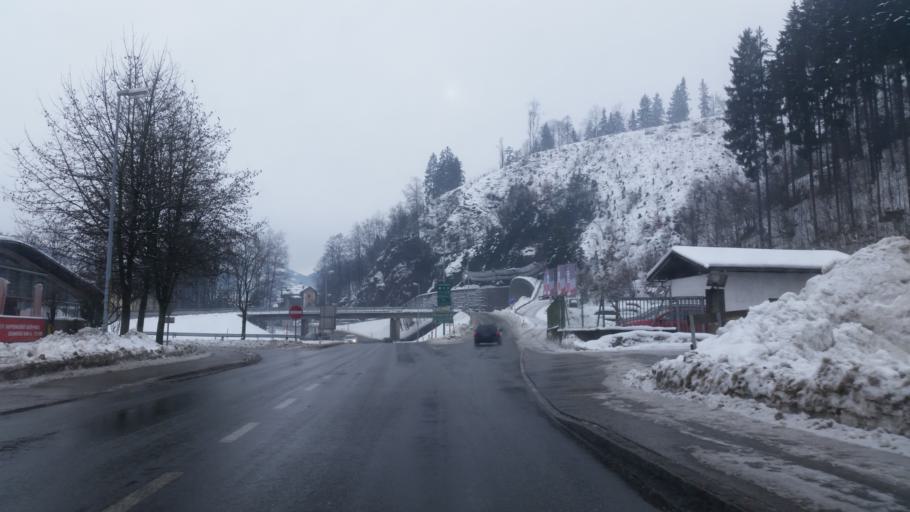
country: AT
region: Tyrol
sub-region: Politischer Bezirk Kitzbuhel
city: Kitzbuhel
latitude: 47.4552
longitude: 12.3870
